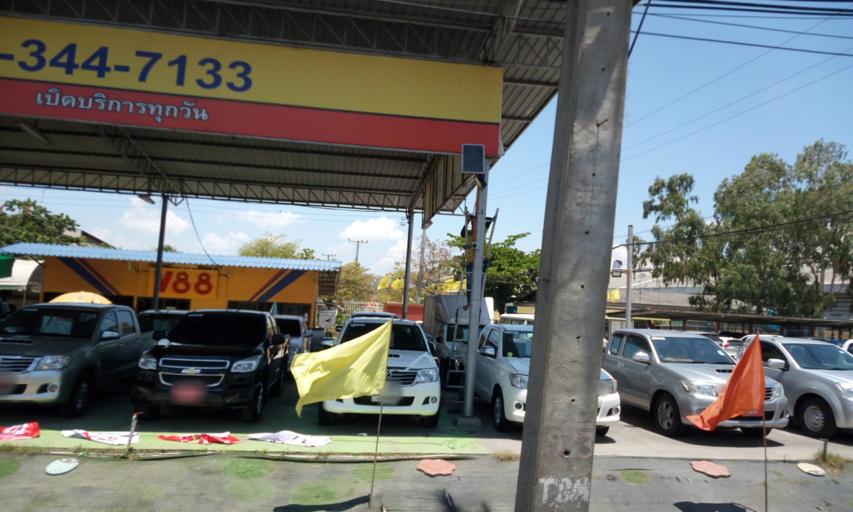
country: TH
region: Bangkok
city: Bang Na
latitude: 13.6189
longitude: 100.7043
